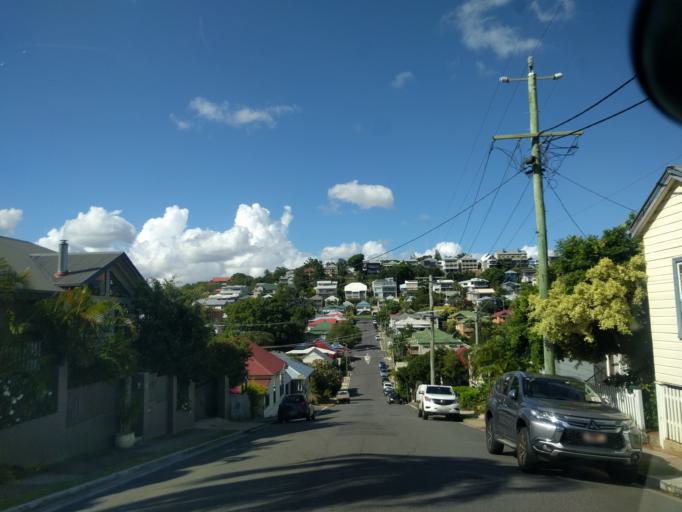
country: AU
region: Queensland
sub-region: Brisbane
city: Milton
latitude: -27.4612
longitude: 153.0057
